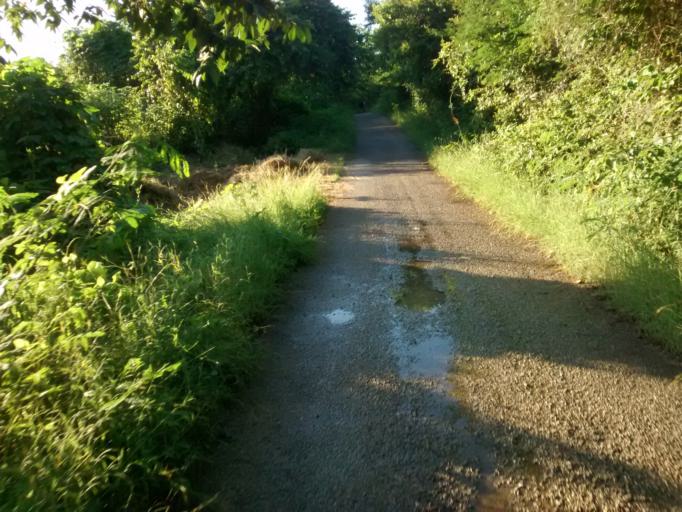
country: MX
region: Yucatan
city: Valladolid
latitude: 20.7129
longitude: -88.2194
